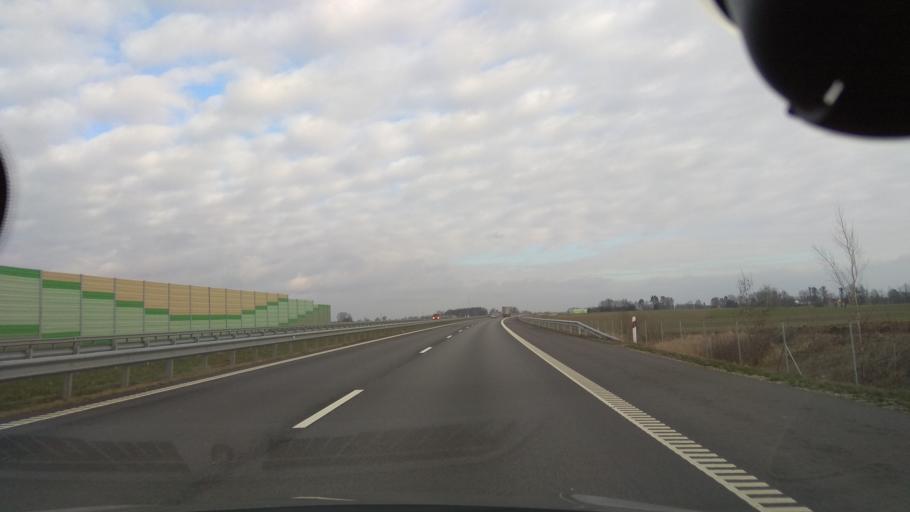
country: LT
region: Kauno apskritis
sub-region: Kauno rajonas
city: Mastaiciai
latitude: 54.7515
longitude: 23.7289
